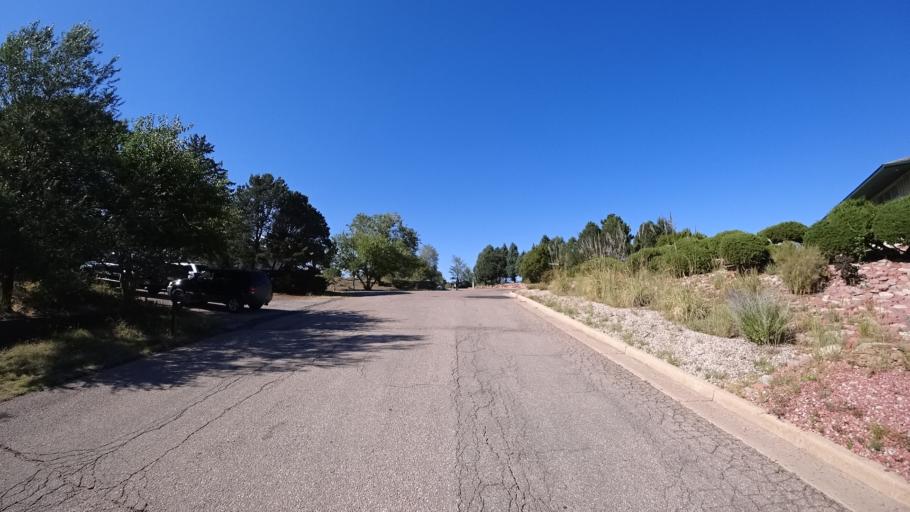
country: US
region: Colorado
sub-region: El Paso County
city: Colorado Springs
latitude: 38.8522
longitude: -104.8390
